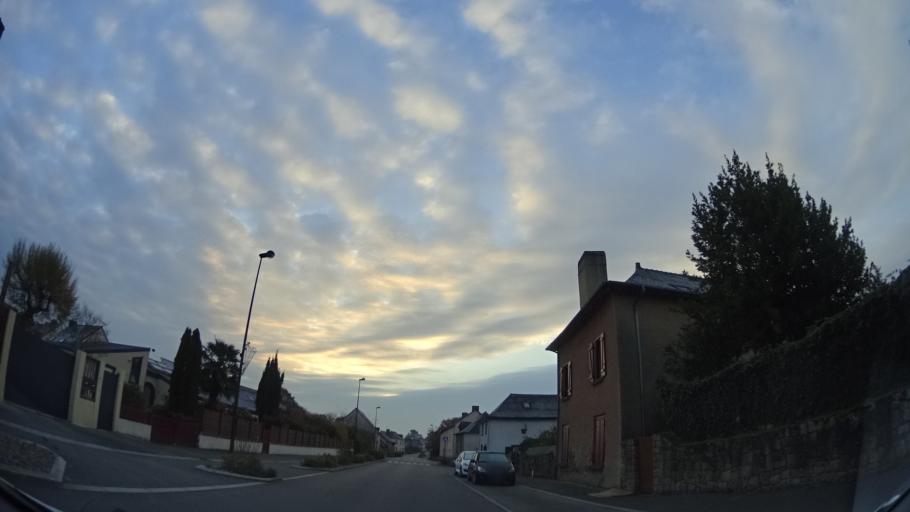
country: FR
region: Brittany
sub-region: Departement d'Ille-et-Vilaine
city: La Meziere
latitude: 48.2013
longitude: -1.7374
